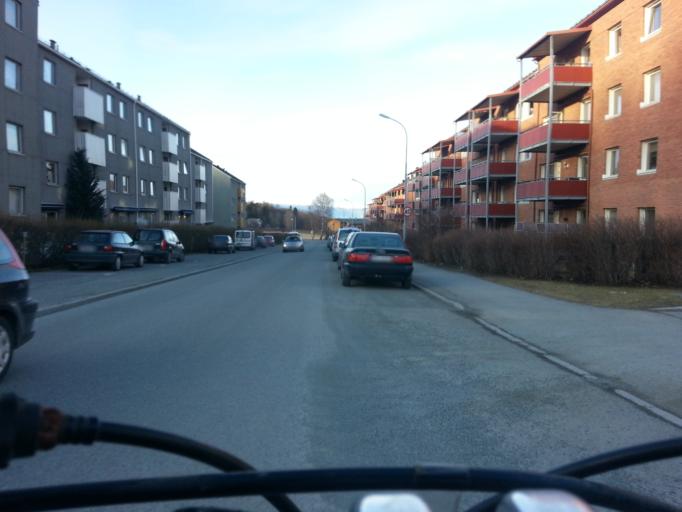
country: NO
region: Sor-Trondelag
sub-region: Trondheim
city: Trondheim
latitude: 63.4475
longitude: 10.4577
